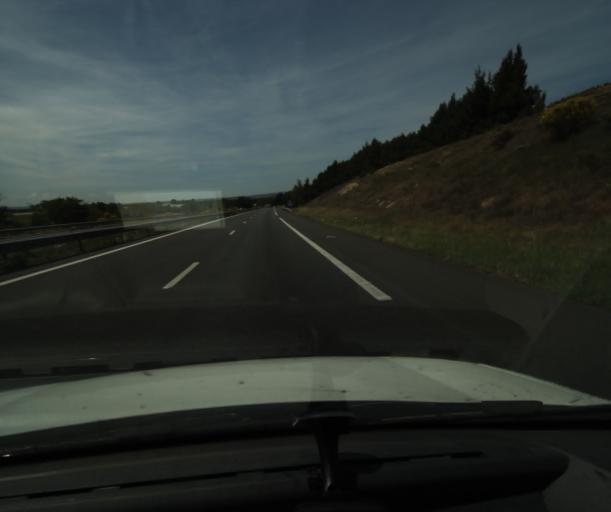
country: FR
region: Languedoc-Roussillon
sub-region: Departement de l'Aude
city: Arzens
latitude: 43.2090
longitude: 2.2379
